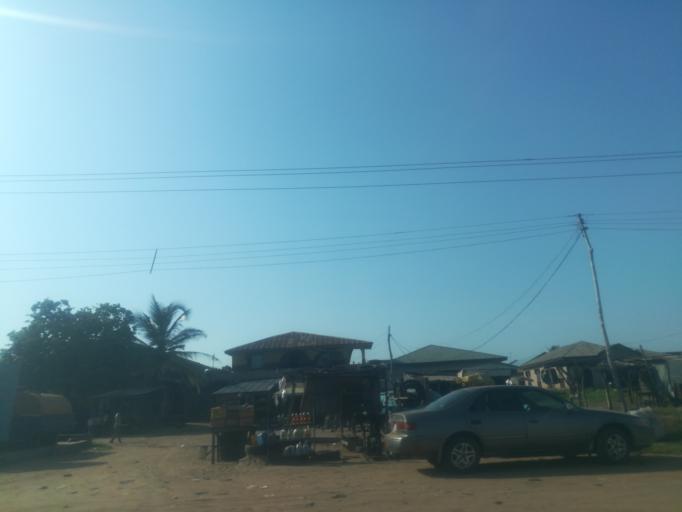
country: NG
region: Ogun
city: Abeokuta
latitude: 7.1681
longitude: 3.2708
